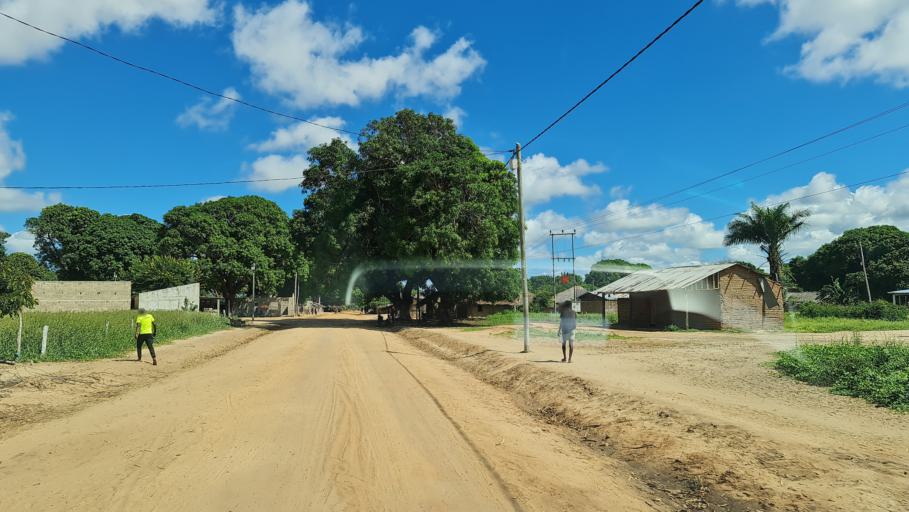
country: MZ
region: Nampula
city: Ilha de Mocambique
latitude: -15.5491
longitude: 40.4054
